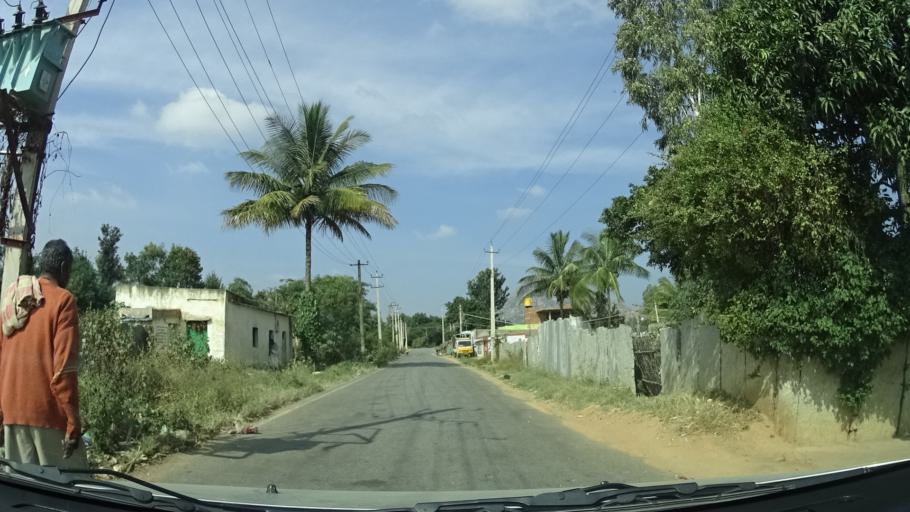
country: IN
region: Karnataka
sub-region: Chikkaballapur
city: Chik Ballapur
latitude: 13.4049
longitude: 77.7200
